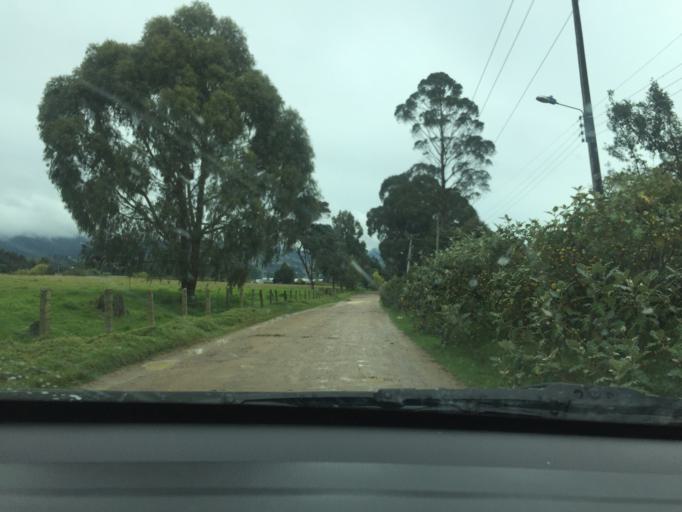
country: CO
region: Cundinamarca
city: El Rosal
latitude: 4.8074
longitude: -74.2834
